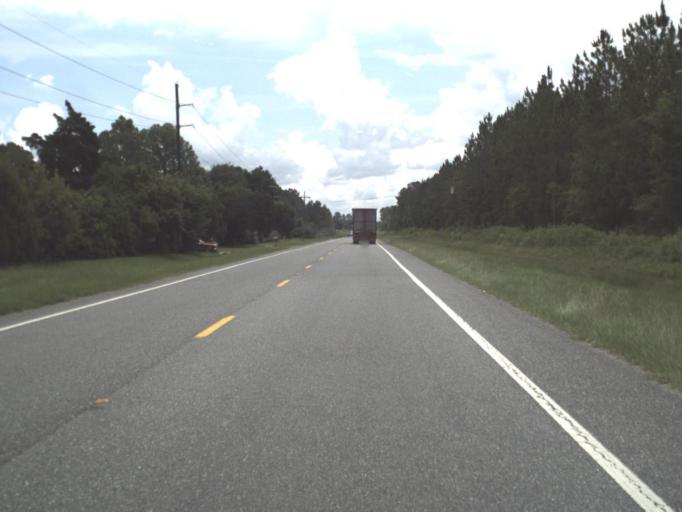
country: US
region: Florida
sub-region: Bradford County
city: Starke
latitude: 29.9602
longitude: -82.1665
